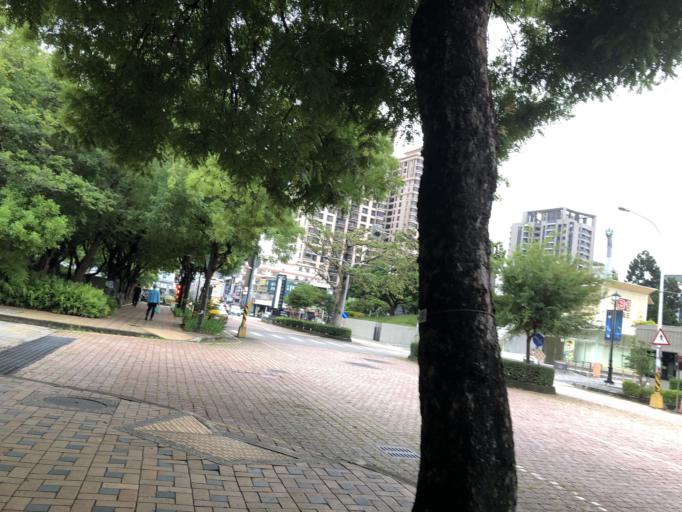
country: TW
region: Taiwan
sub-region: Taichung City
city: Taichung
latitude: 24.1574
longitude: 120.6677
